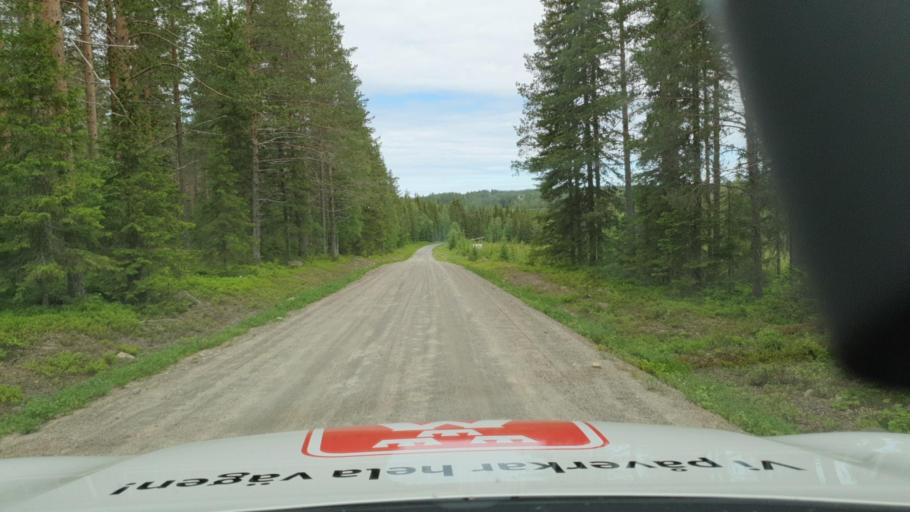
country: SE
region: Vaesterbotten
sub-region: Skelleftea Kommun
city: Langsele
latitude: 64.4653
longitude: 20.2733
